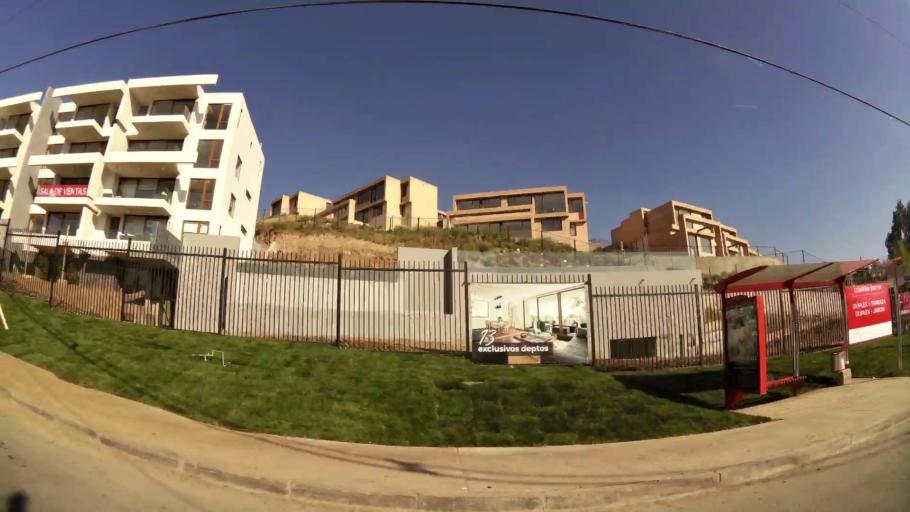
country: CL
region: Santiago Metropolitan
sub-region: Provincia de Santiago
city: Villa Presidente Frei, Nunoa, Santiago, Chile
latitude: -33.3668
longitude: -70.4954
